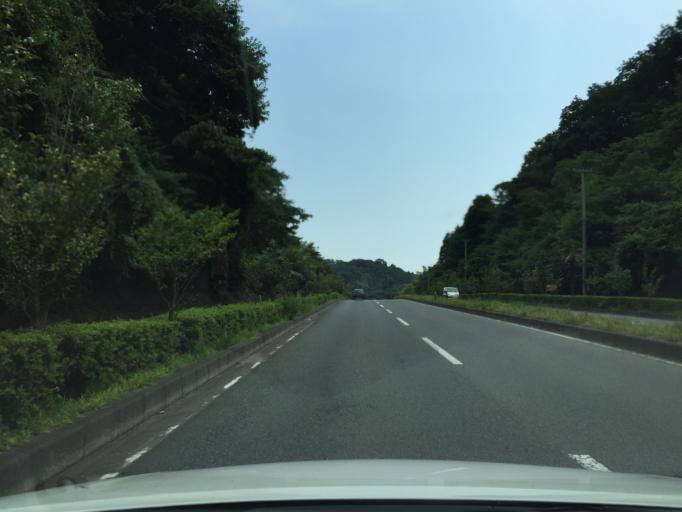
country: JP
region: Fukushima
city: Iwaki
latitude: 36.9709
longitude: 140.9135
